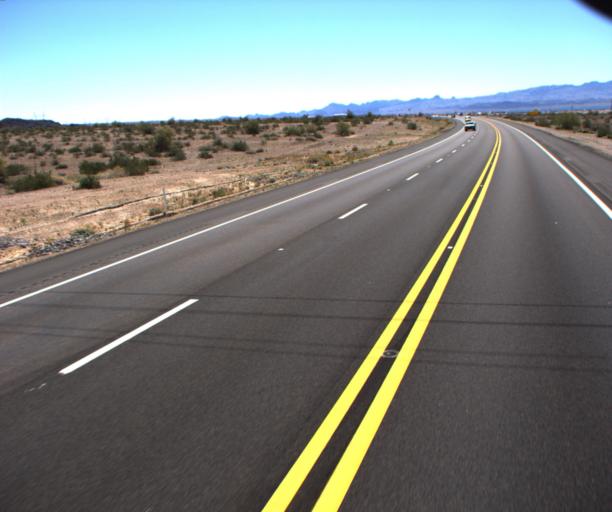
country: US
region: Arizona
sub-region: Mohave County
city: Desert Hills
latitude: 34.5900
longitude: -114.3698
